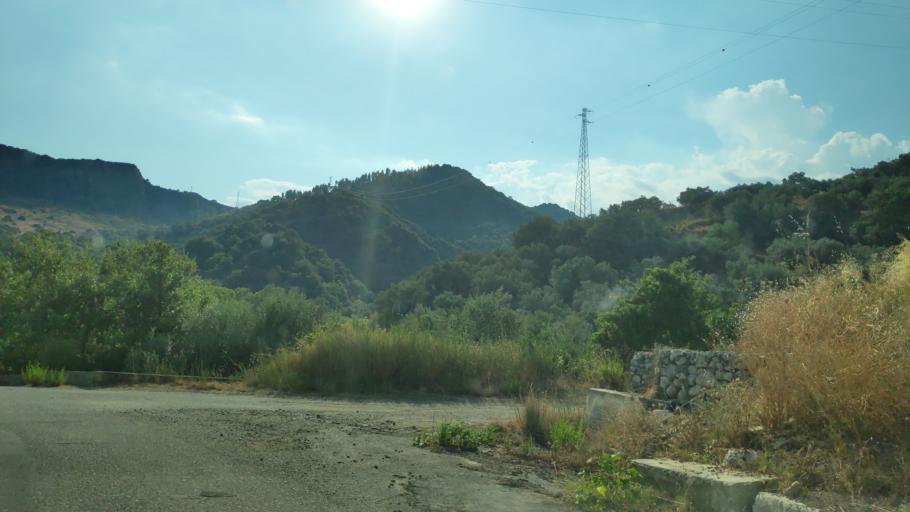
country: IT
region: Calabria
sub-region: Provincia di Reggio Calabria
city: Placanica
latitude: 38.4140
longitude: 16.4418
